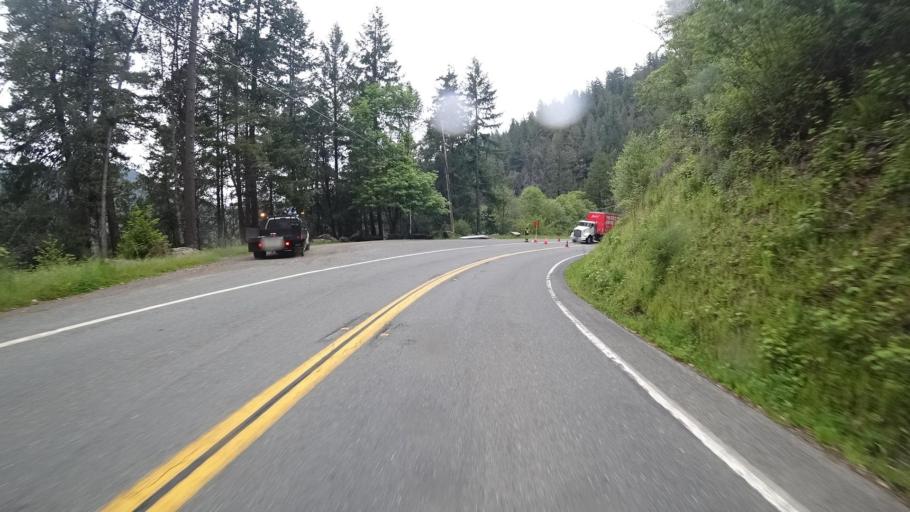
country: US
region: California
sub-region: Humboldt County
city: Willow Creek
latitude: 41.1228
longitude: -123.6859
